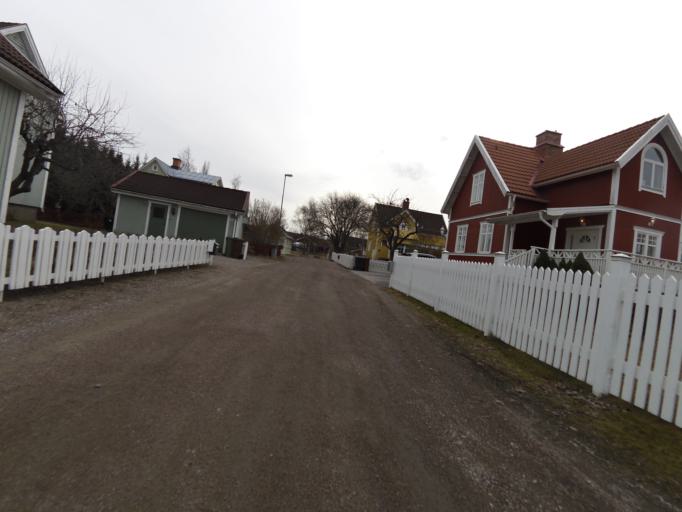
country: SE
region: Gaevleborg
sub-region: Gavle Kommun
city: Gavle
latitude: 60.6560
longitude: 17.1608
